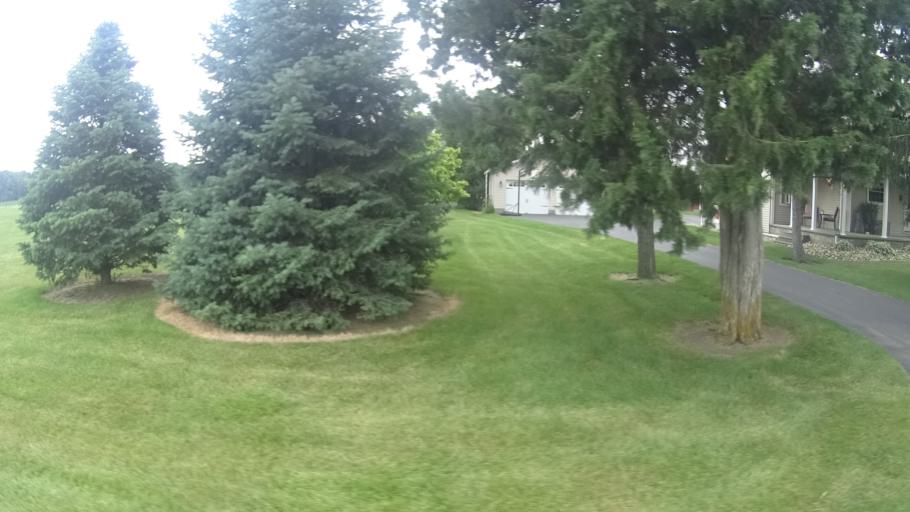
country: US
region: Ohio
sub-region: Huron County
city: Monroeville
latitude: 41.3088
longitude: -82.6738
